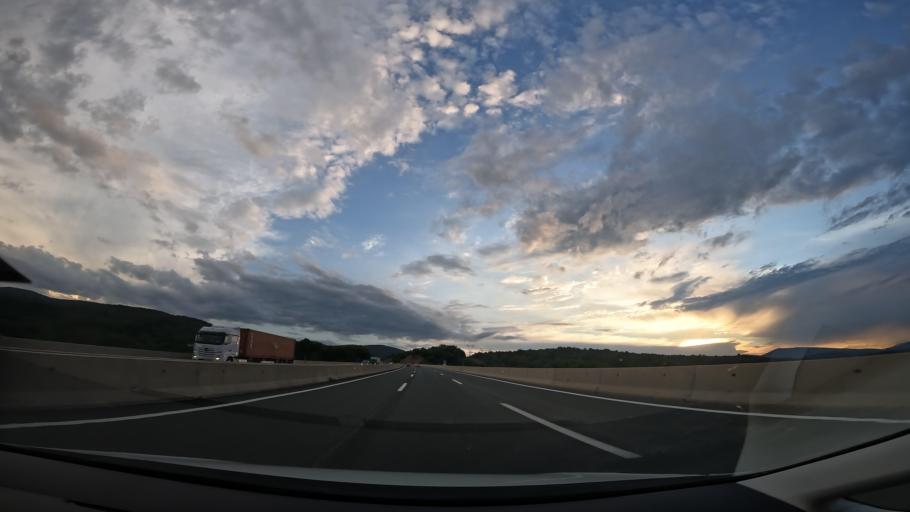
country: HR
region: Karlovacka
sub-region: Grad Ogulin
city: Ogulin
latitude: 45.3988
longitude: 15.2111
